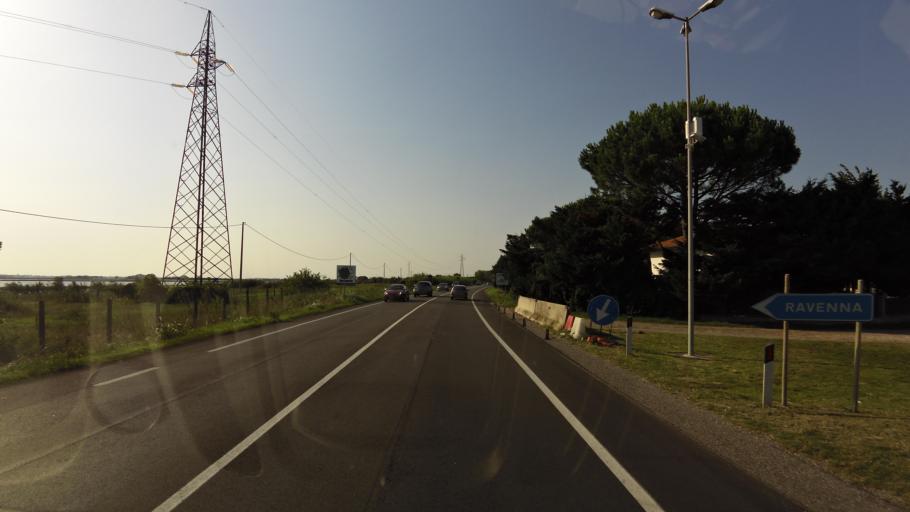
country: IT
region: Emilia-Romagna
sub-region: Provincia di Ravenna
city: Cervia
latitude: 44.2398
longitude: 12.3545
